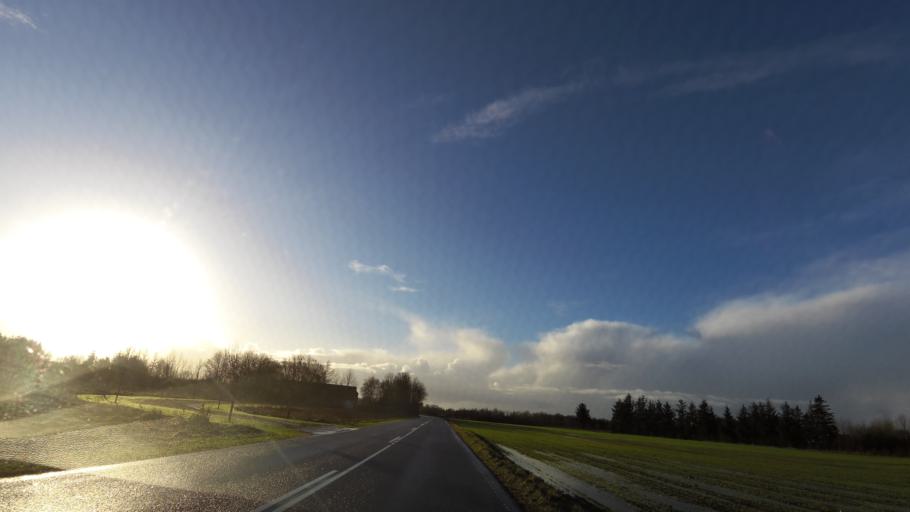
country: DK
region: Central Jutland
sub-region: Ikast-Brande Kommune
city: Ikast
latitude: 56.0600
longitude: 9.1406
